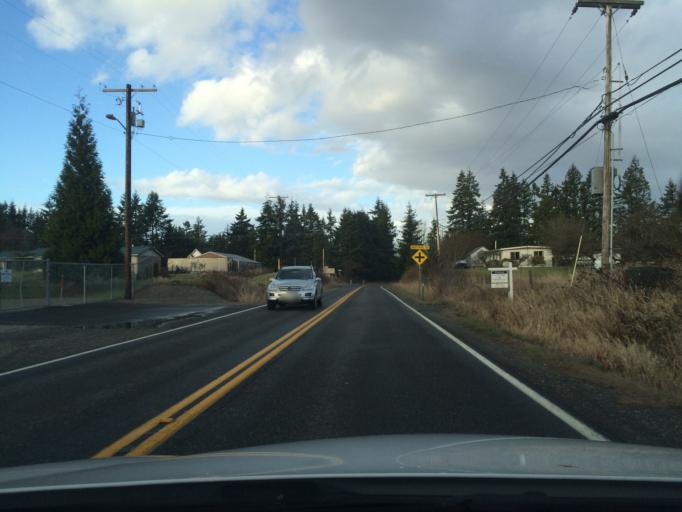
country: US
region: Washington
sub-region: Whatcom County
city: Blaine
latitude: 48.9696
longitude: -122.7299
